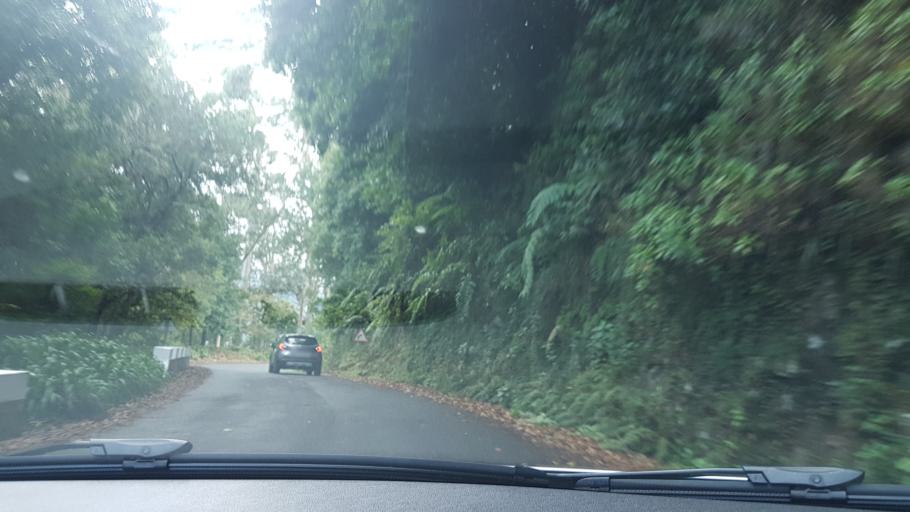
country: PT
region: Madeira
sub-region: Sao Vicente
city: Sao Vicente
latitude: 32.7642
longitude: -17.0225
